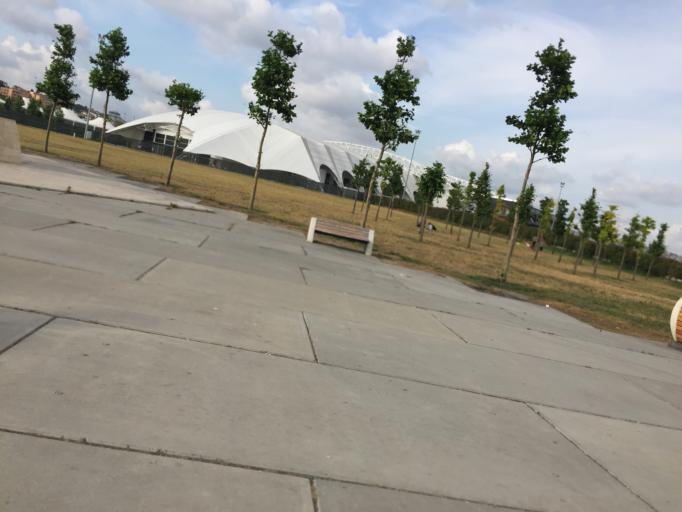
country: TR
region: Istanbul
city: Istanbul
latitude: 40.9972
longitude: 28.9416
